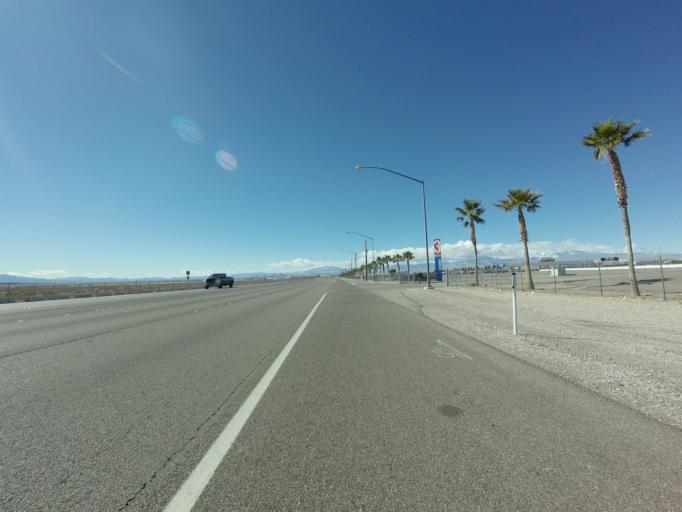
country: US
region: Nevada
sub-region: Clark County
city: Nellis Air Force Base
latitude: 36.2638
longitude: -115.0147
